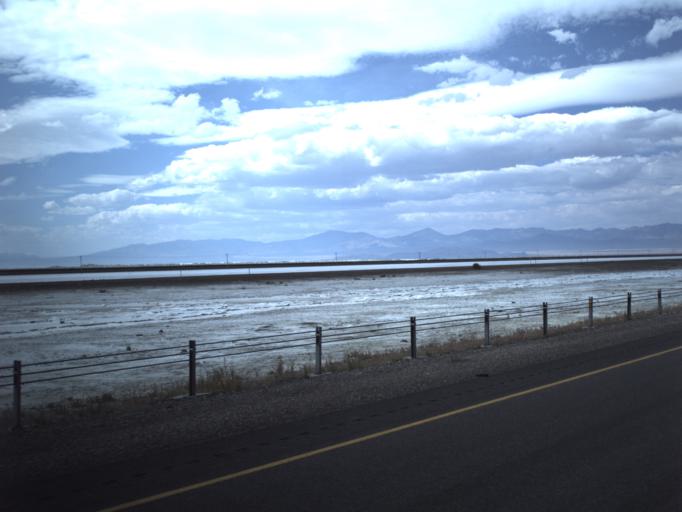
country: US
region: Utah
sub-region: Tooele County
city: Wendover
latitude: 40.7398
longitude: -113.8721
